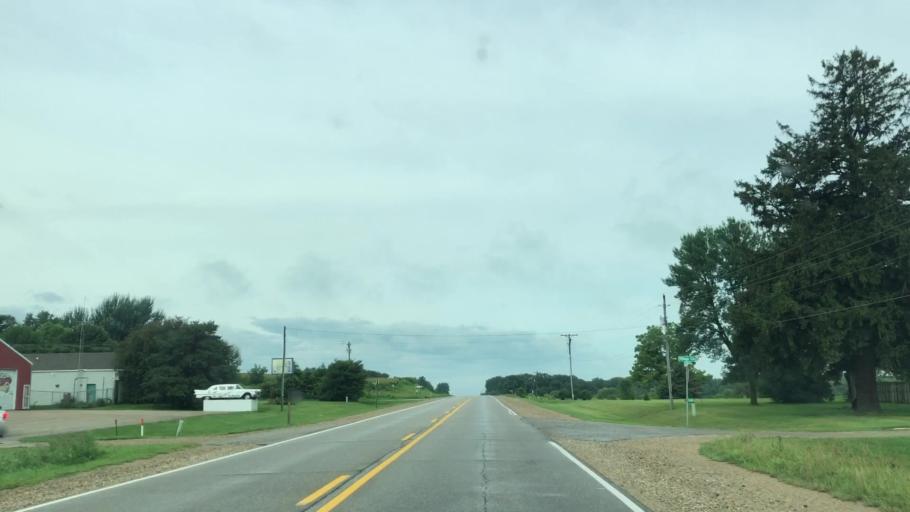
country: US
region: Iowa
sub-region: Marshall County
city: Marshalltown
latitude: 42.0075
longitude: -92.9398
